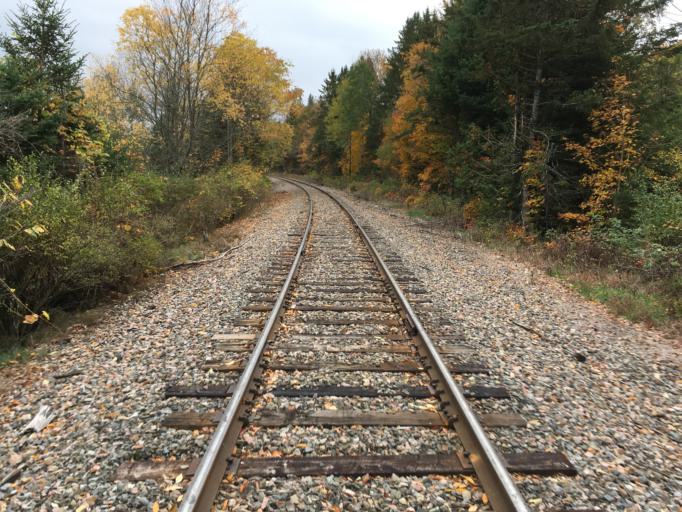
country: US
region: Vermont
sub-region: Caledonia County
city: Lyndonville
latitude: 44.6357
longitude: -71.9795
